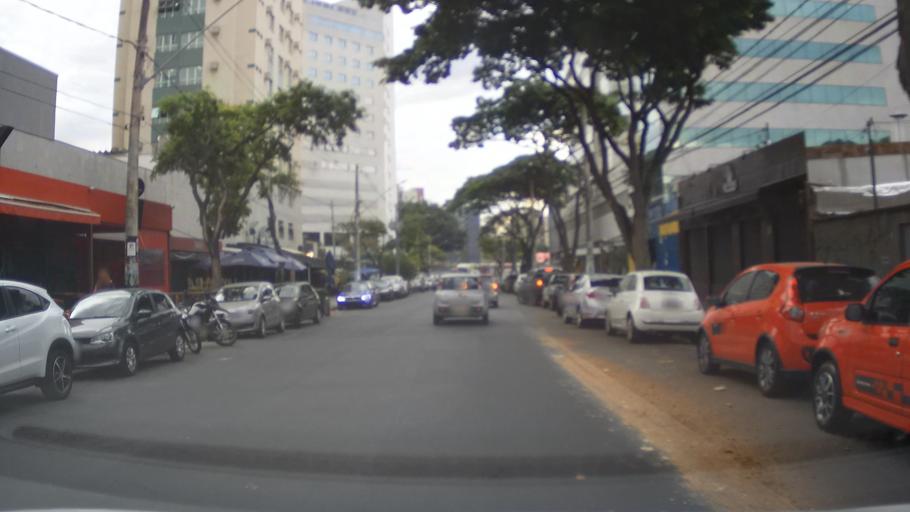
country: BR
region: Minas Gerais
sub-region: Belo Horizonte
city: Belo Horizonte
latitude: -19.8803
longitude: -43.9284
